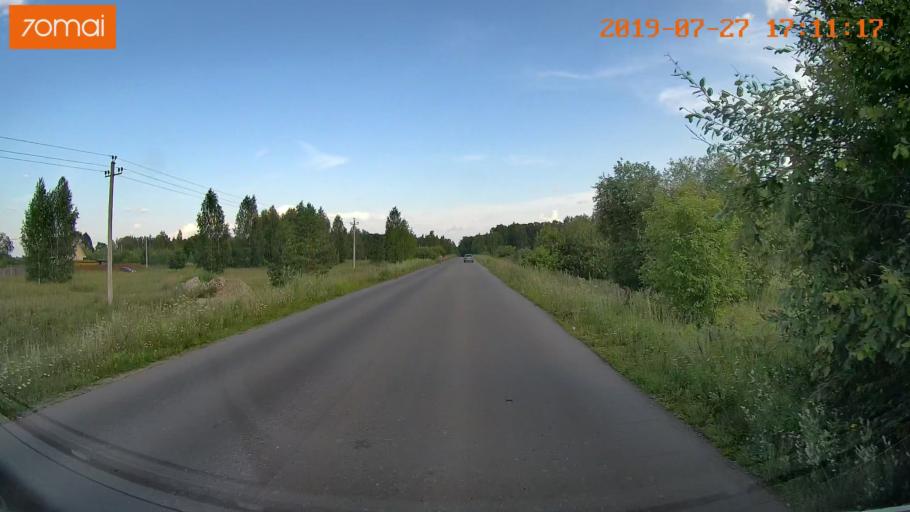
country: RU
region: Ivanovo
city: Novo-Talitsy
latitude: 57.0658
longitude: 40.8594
